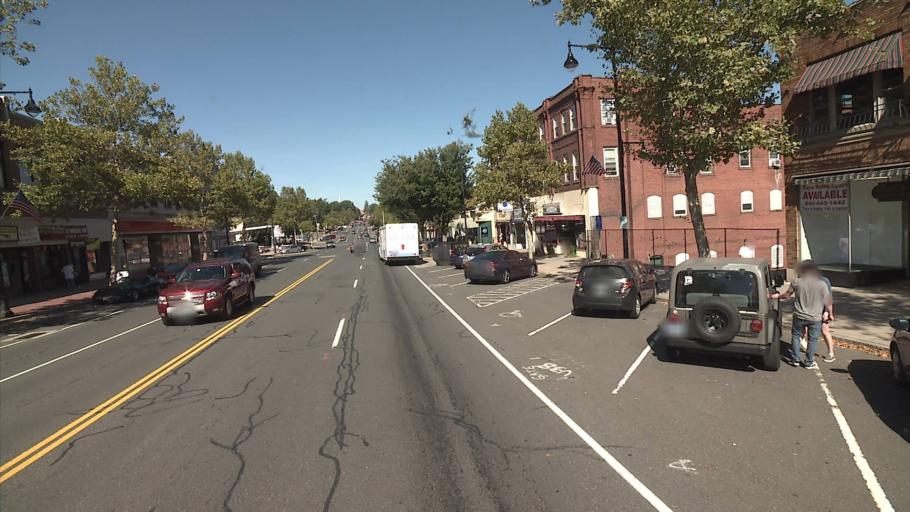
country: US
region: Connecticut
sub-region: Hartford County
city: Manchester
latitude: 41.7709
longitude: -72.5209
